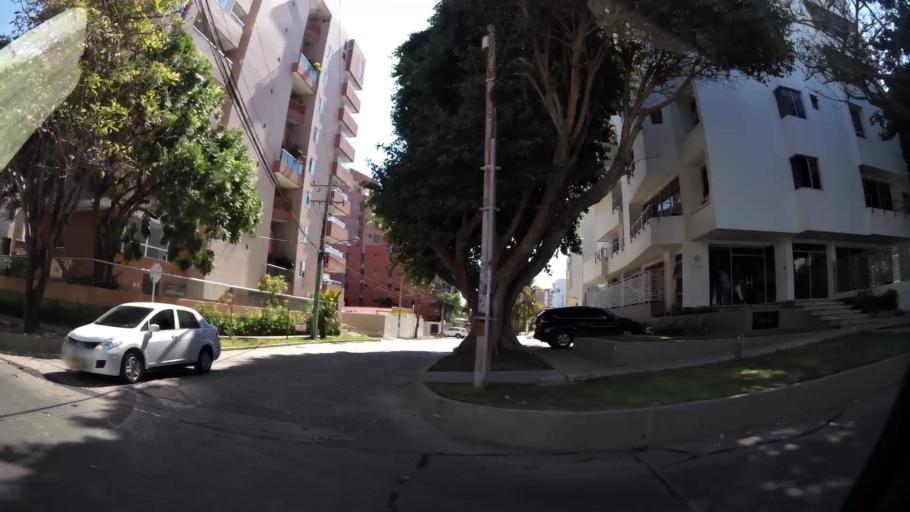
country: CO
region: Atlantico
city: Barranquilla
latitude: 11.0143
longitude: -74.8121
